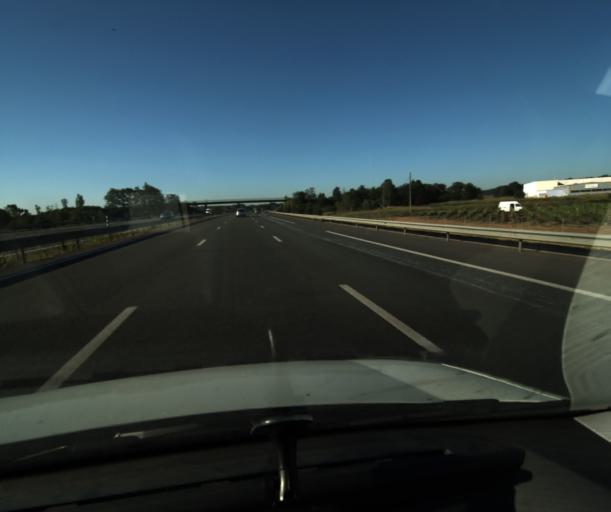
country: FR
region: Midi-Pyrenees
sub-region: Departement du Tarn-et-Garonne
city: Campsas
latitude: 43.9138
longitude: 1.3191
